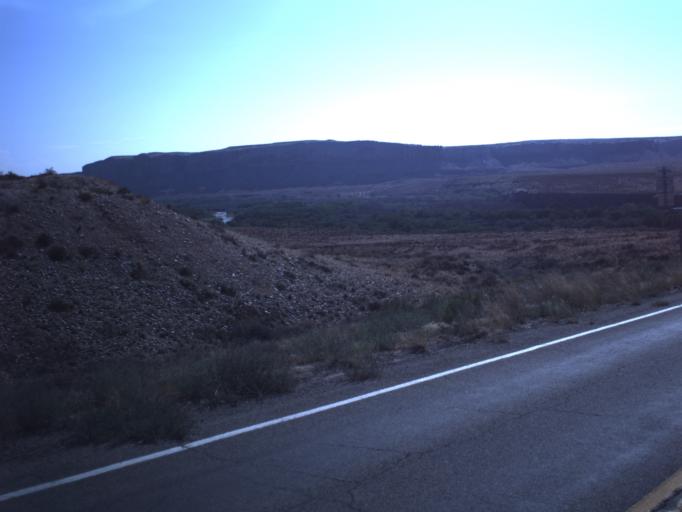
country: US
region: Utah
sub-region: San Juan County
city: Blanding
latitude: 37.2629
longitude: -109.6244
